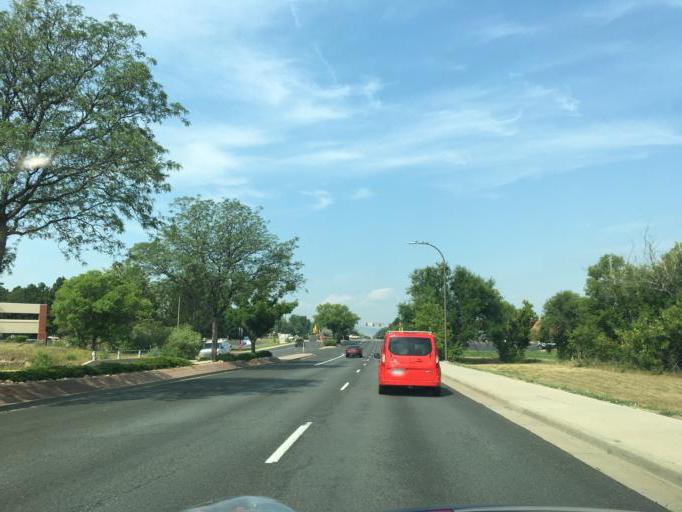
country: US
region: Colorado
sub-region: Jefferson County
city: Arvada
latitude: 39.8420
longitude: -105.1073
